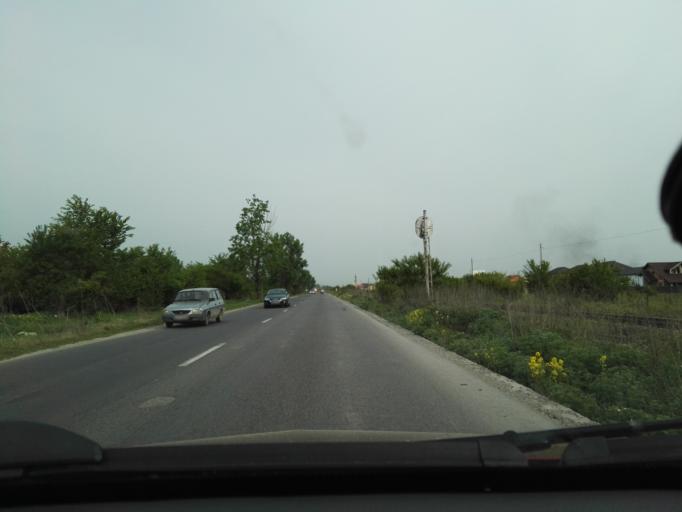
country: RO
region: Ilfov
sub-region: Comuna Magurele
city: Varteju
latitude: 44.3747
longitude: 26.0064
